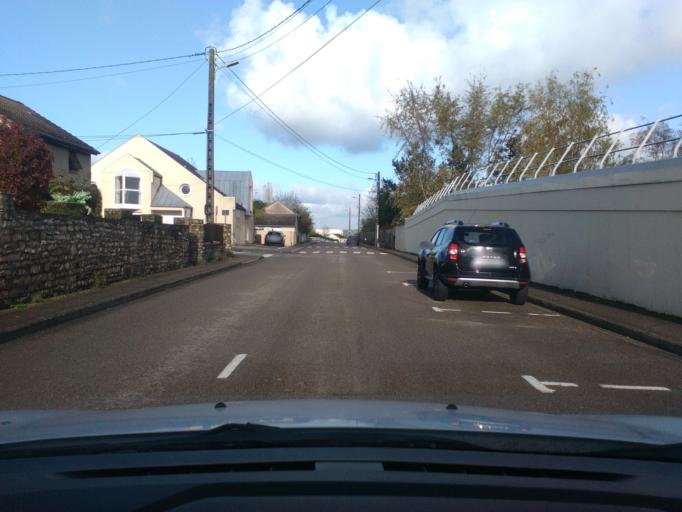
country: FR
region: Lorraine
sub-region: Departement des Vosges
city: Mirecourt
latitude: 48.3041
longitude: 6.1312
